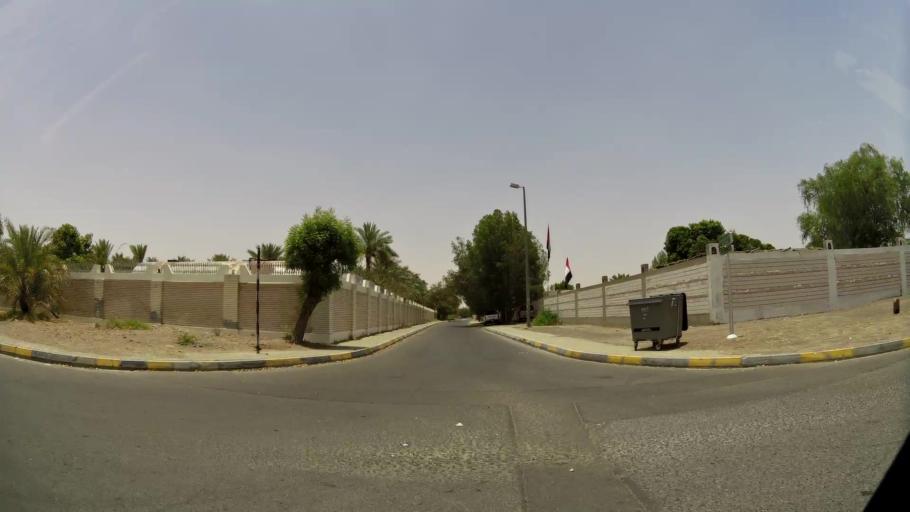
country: AE
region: Abu Dhabi
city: Al Ain
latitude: 24.2163
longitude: 55.7144
